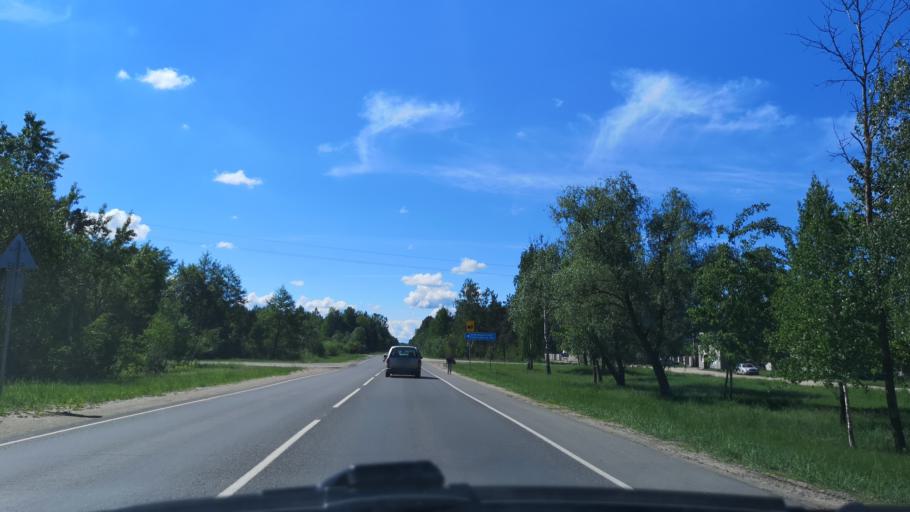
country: BY
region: Brest
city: Brest
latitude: 52.0399
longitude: 23.7282
